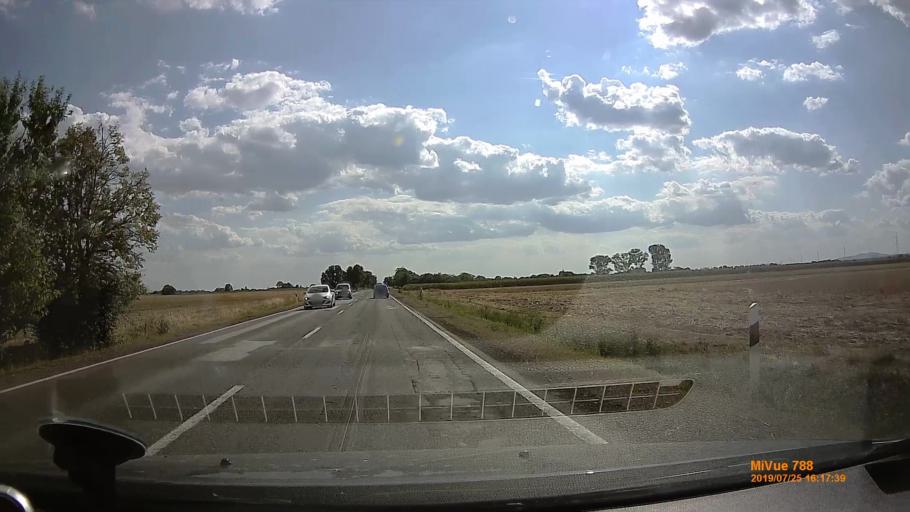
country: HU
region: Heves
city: Kal
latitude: 47.7672
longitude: 20.2718
